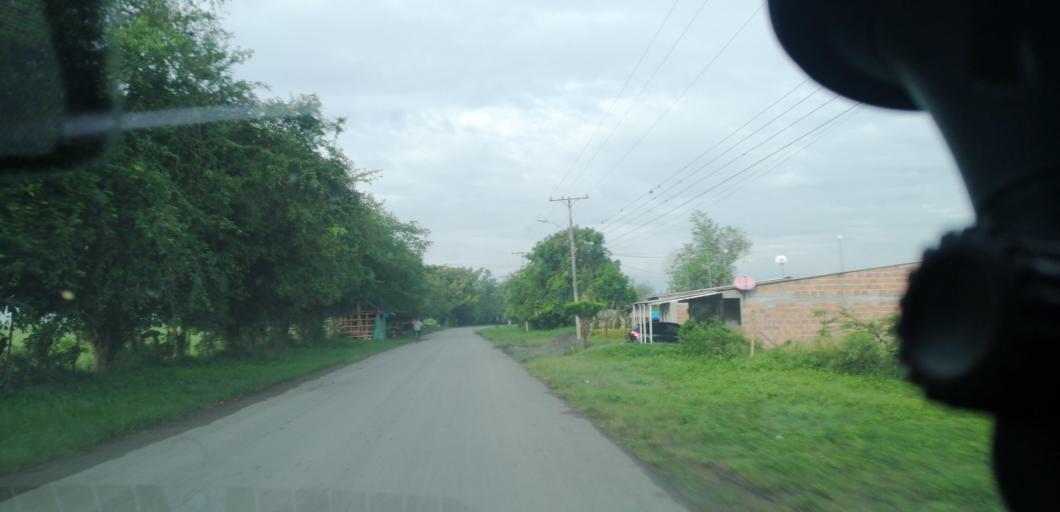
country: CO
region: Valle del Cauca
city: Palmira
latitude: 3.5367
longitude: -76.3546
